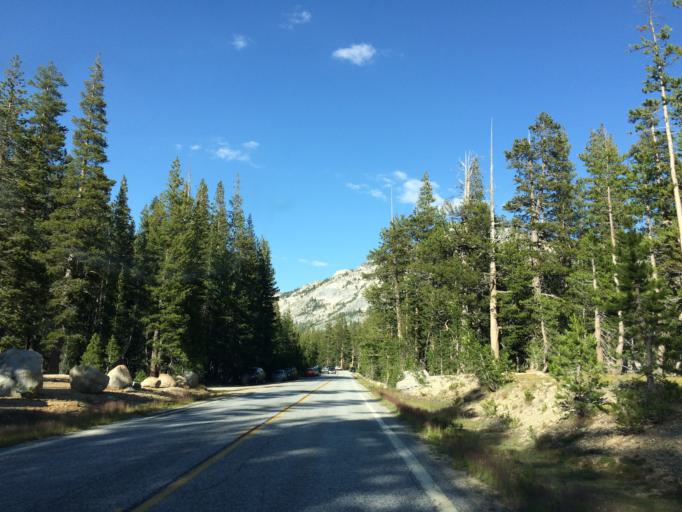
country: US
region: California
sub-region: Mariposa County
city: Yosemite Valley
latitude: 37.8253
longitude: -119.4726
